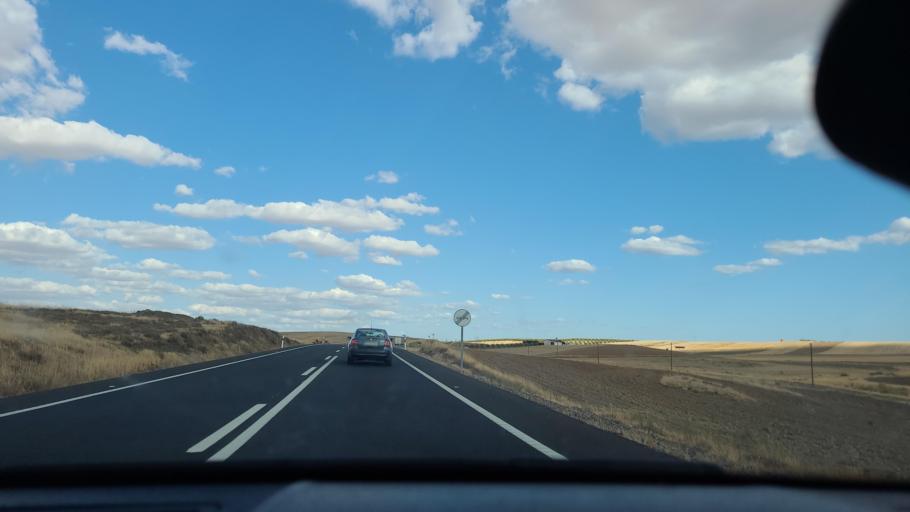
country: ES
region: Extremadura
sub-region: Provincia de Badajoz
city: Berlanga
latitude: 38.2713
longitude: -5.7971
